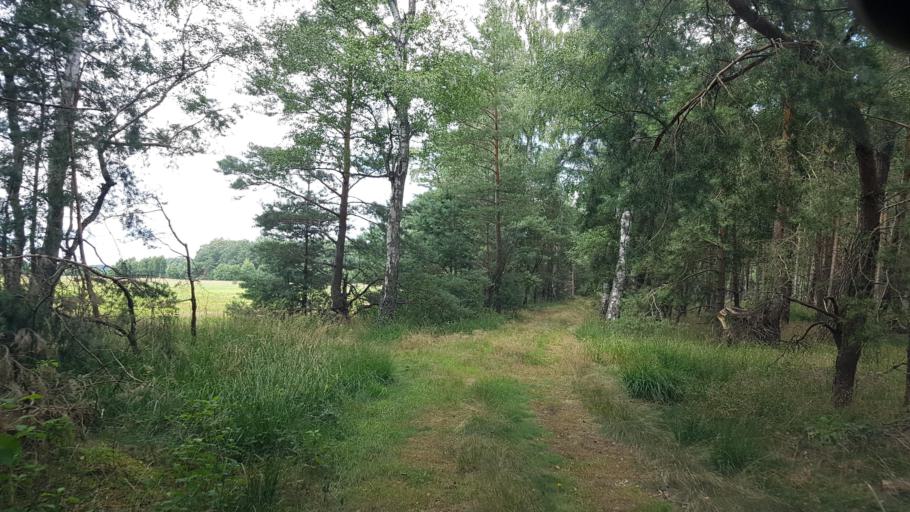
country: DE
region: Brandenburg
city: Trobitz
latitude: 51.6372
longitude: 13.4172
